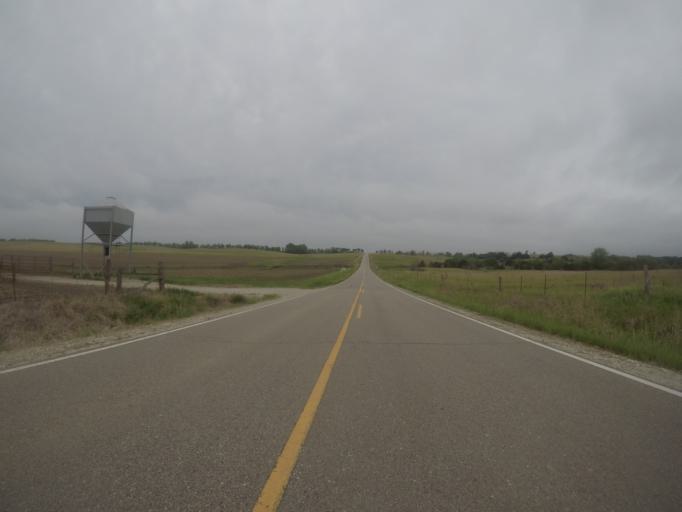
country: US
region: Kansas
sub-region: Pottawatomie County
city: Westmoreland
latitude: 39.5207
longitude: -96.2395
